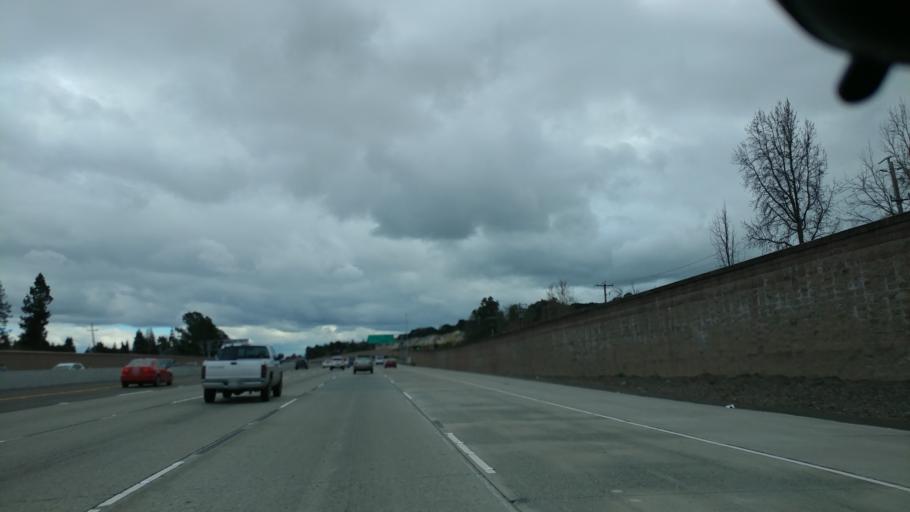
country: US
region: California
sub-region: Contra Costa County
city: Danville
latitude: 37.8034
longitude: -121.9897
